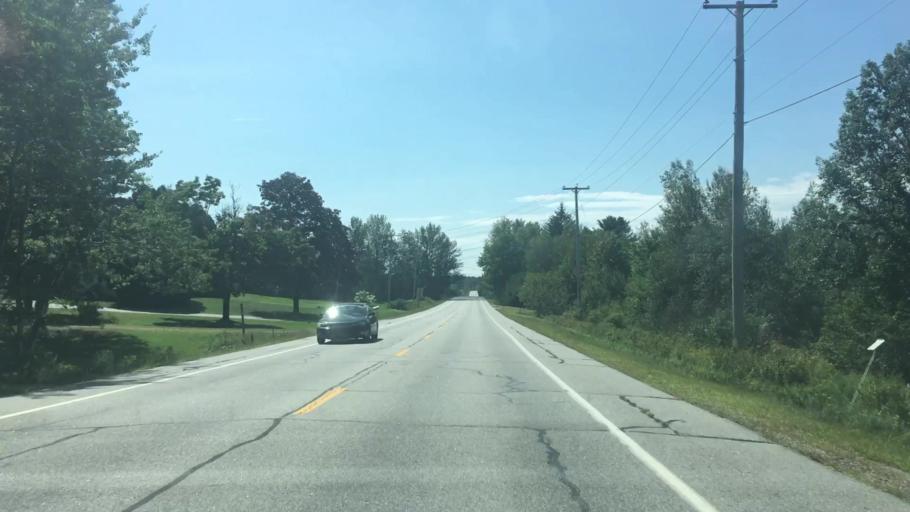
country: US
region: Maine
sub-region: Kennebec County
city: Monmouth
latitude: 44.1802
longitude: -69.9948
